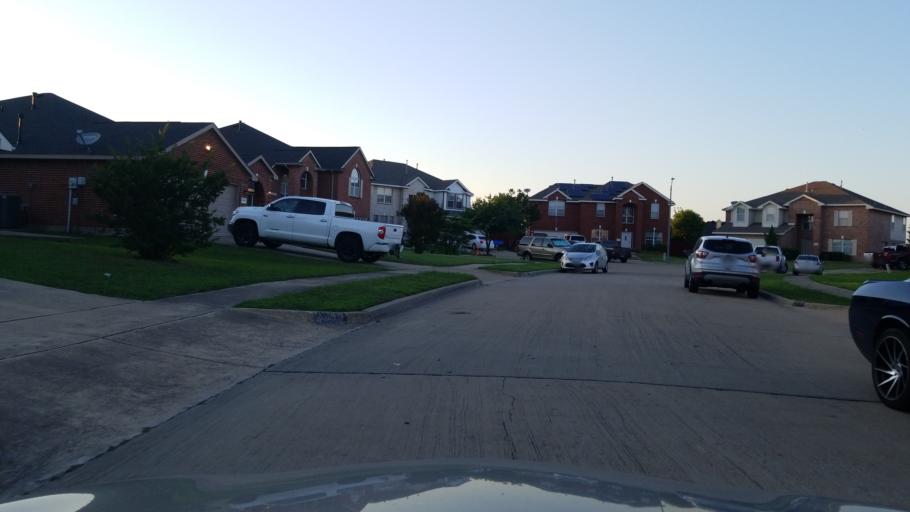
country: US
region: Texas
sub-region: Dallas County
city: Grand Prairie
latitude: 32.6878
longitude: -97.0399
